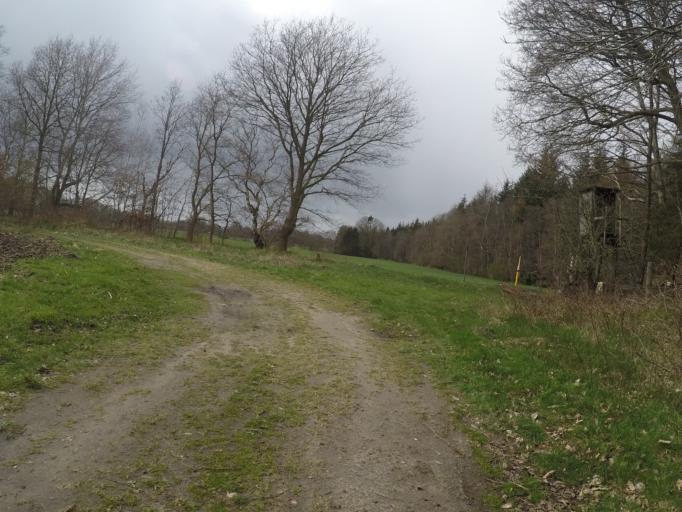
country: DE
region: Lower Saxony
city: Elmlohe
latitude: 53.6246
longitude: 8.6760
